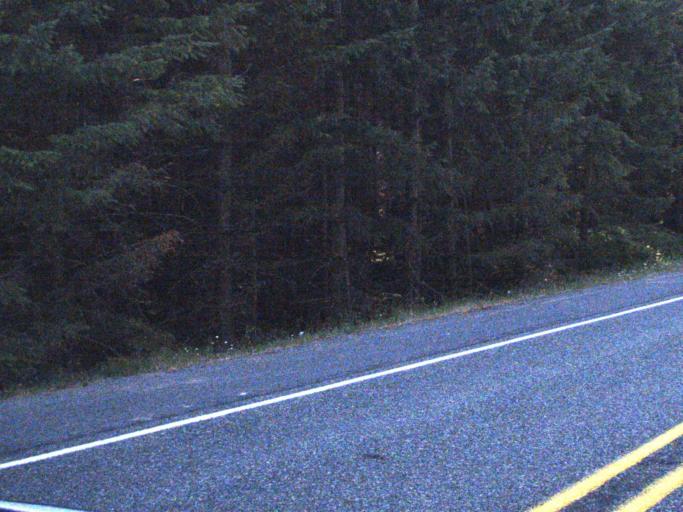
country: US
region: Washington
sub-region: King County
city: Riverbend
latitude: 47.0912
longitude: -121.5841
